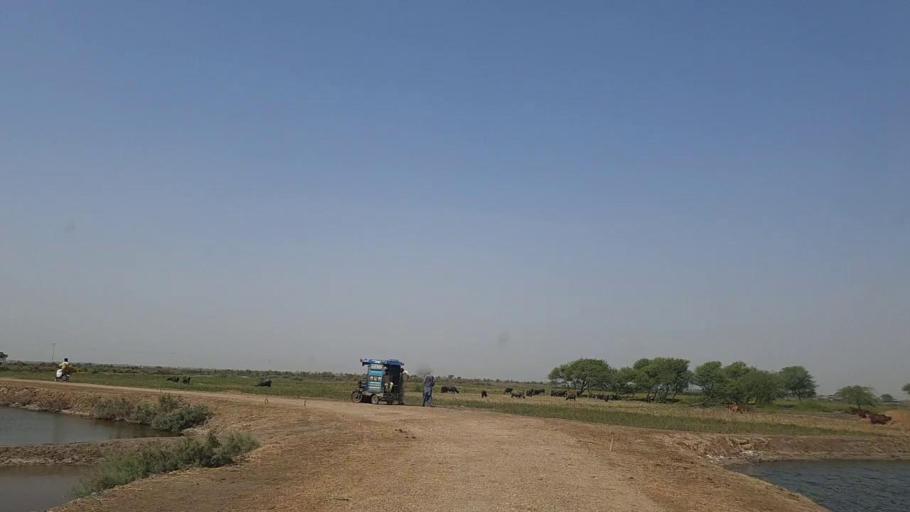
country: PK
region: Sindh
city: Daro Mehar
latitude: 24.7416
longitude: 68.1453
